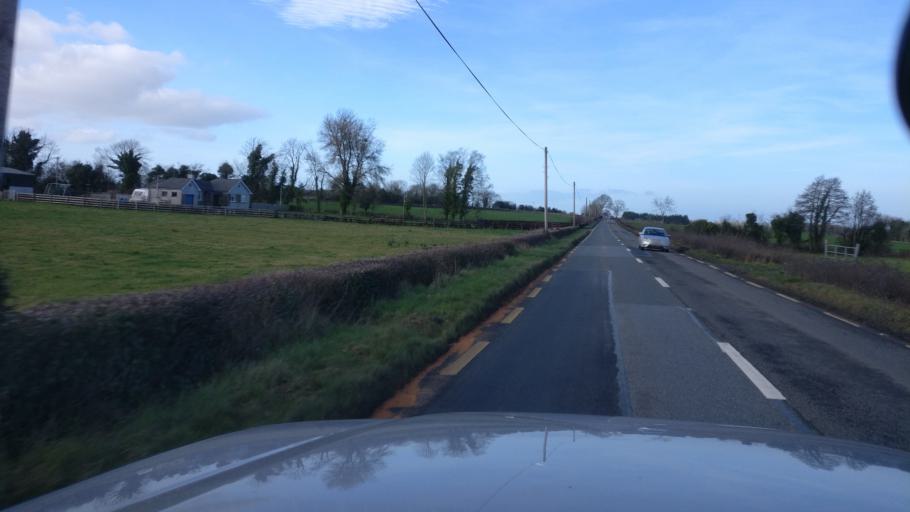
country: IE
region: Leinster
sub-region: Laois
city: Mountmellick
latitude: 53.0939
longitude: -7.3364
